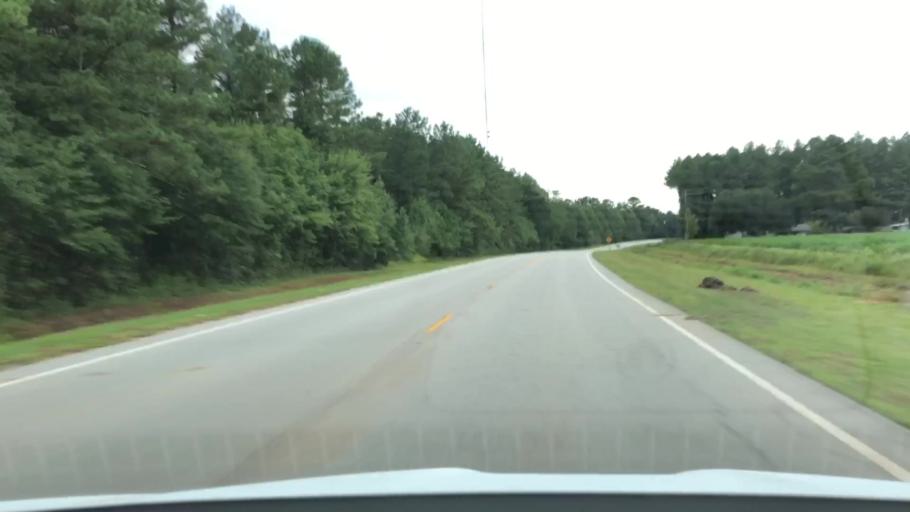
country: US
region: North Carolina
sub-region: Jones County
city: Trenton
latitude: 35.0379
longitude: -77.3460
